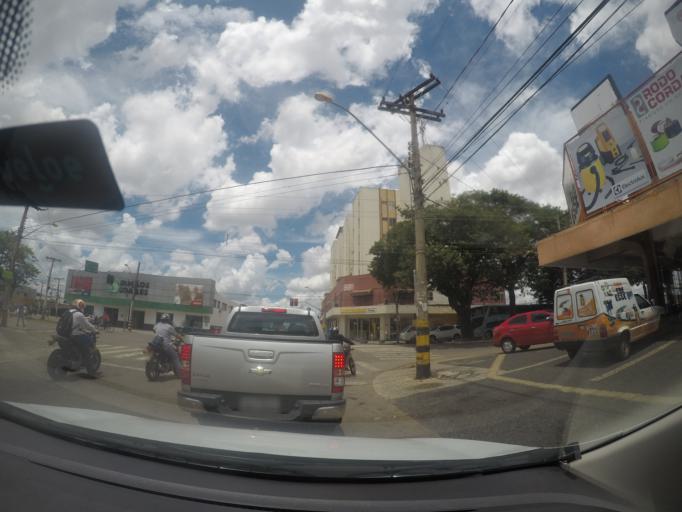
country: BR
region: Goias
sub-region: Goiania
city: Goiania
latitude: -16.6723
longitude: -49.3059
